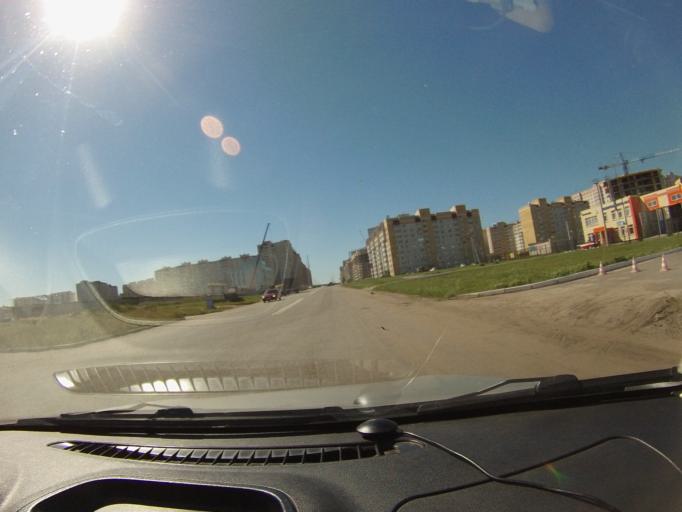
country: RU
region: Tambov
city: Tambov
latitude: 52.7749
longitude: 41.4056
